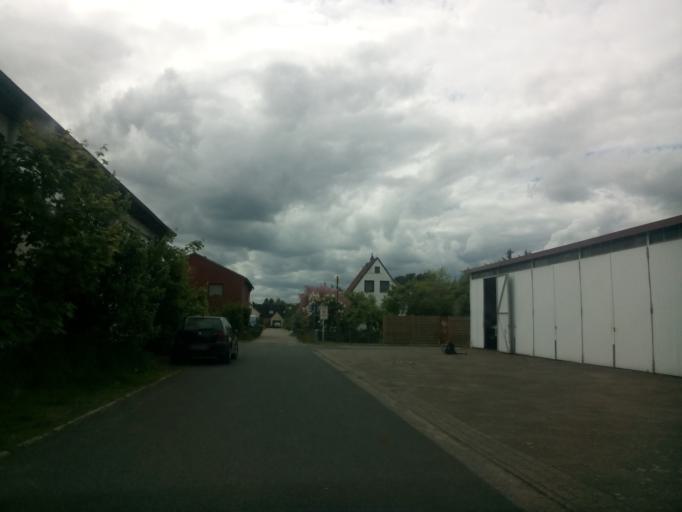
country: DE
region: Lower Saxony
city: Lemwerder
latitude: 53.1501
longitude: 8.6150
